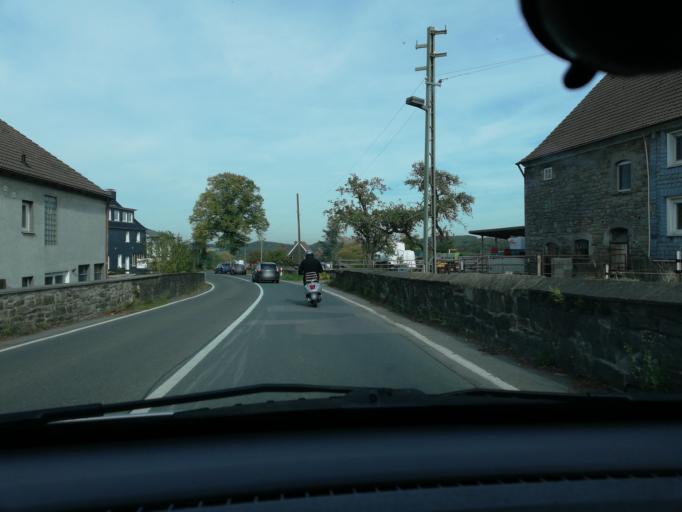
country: DE
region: North Rhine-Westphalia
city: Sprockhovel
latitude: 51.3397
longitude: 7.2587
